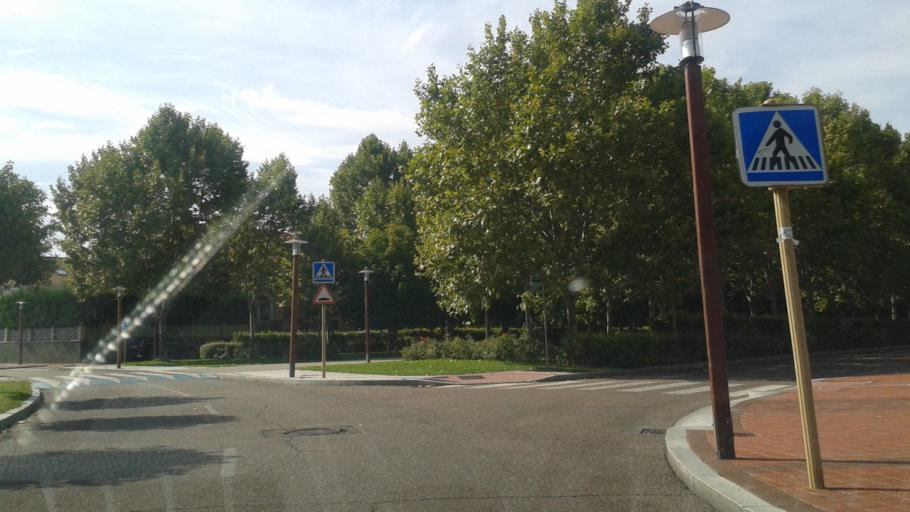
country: ES
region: Castille and Leon
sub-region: Provincia de Valladolid
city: Arroyo
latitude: 41.6129
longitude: -4.7846
